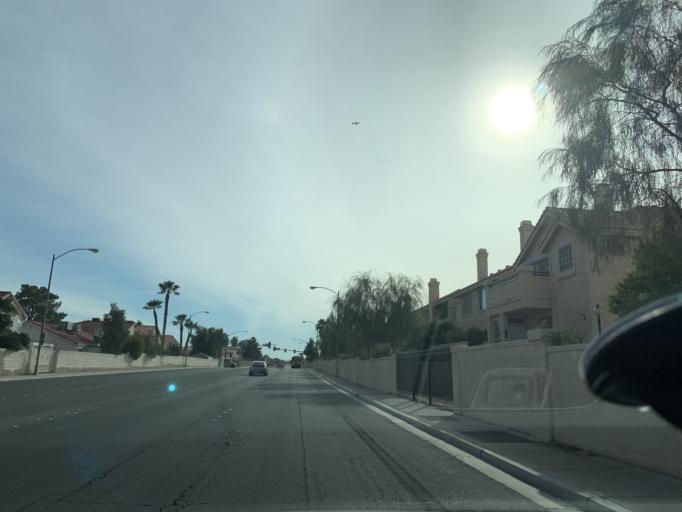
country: US
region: Nevada
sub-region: Clark County
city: Spring Valley
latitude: 36.0941
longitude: -115.2342
